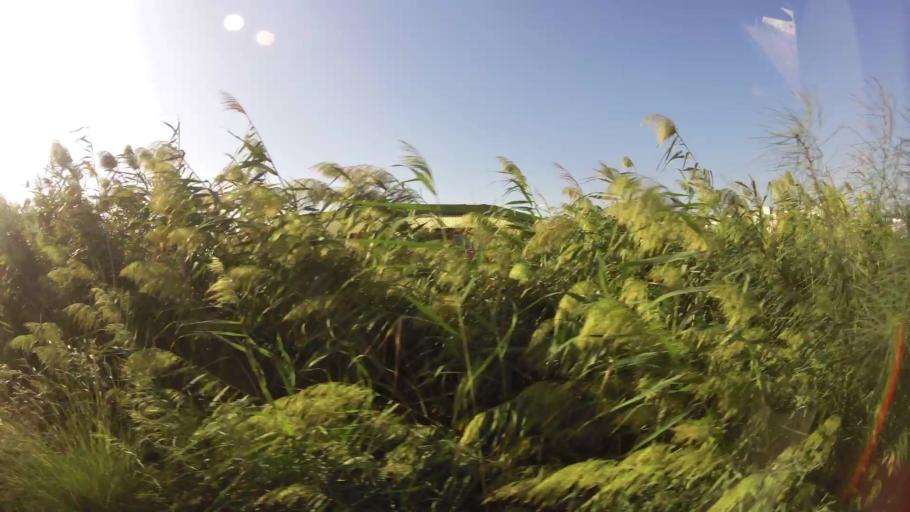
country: CY
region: Lefkosia
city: Nicosia
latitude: 35.2114
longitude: 33.3670
